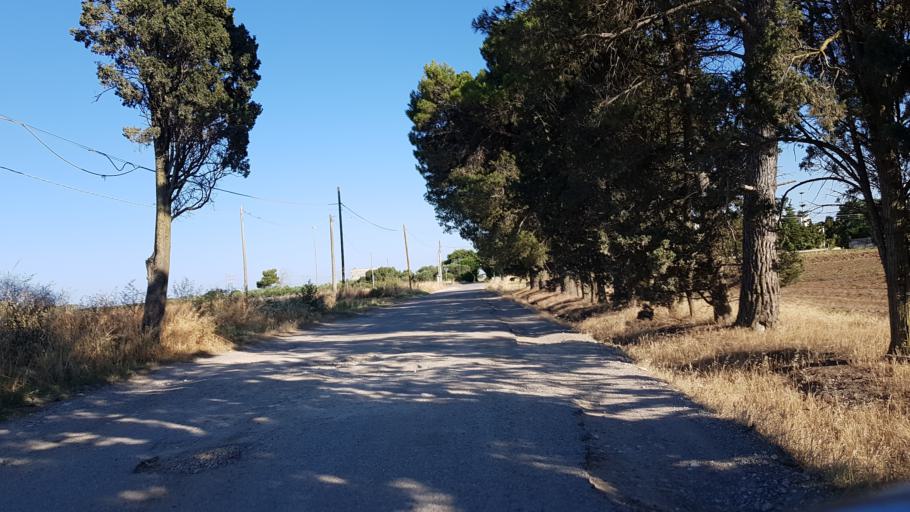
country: IT
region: Apulia
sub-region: Provincia di Brindisi
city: Tuturano
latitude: 40.5638
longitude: 18.0093
